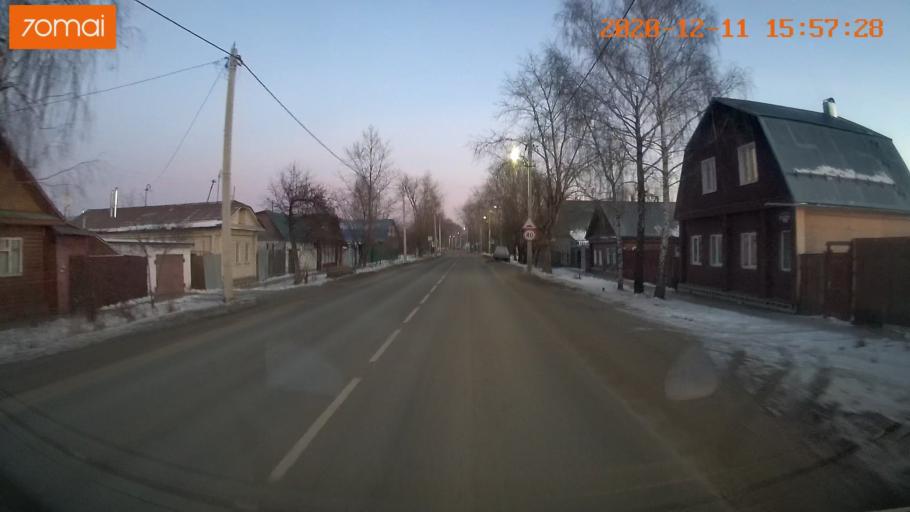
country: RU
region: Ivanovo
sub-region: Gorod Ivanovo
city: Ivanovo
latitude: 56.9817
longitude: 40.9404
